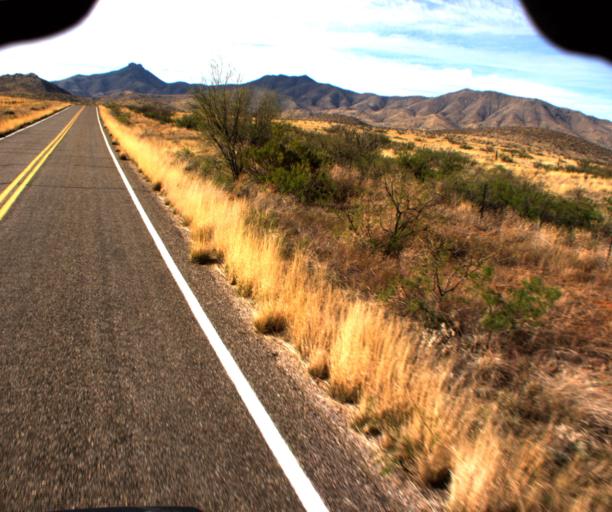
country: US
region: Arizona
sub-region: Cochise County
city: Willcox
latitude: 32.1336
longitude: -109.5600
